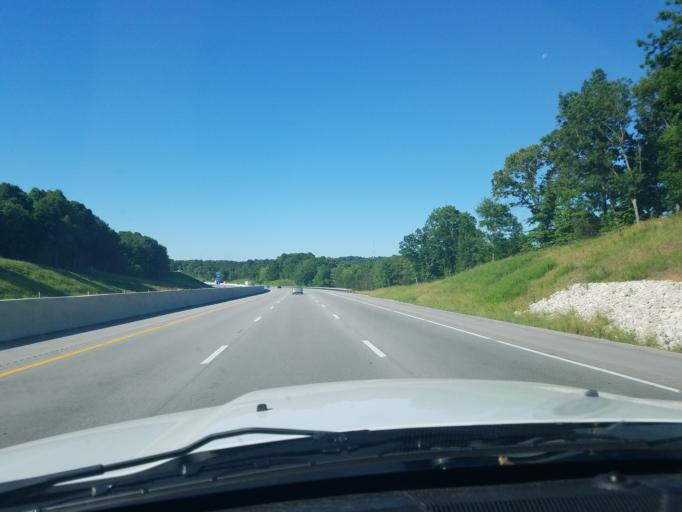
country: US
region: Kentucky
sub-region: Hart County
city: Munfordville
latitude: 37.3419
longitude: -85.9056
